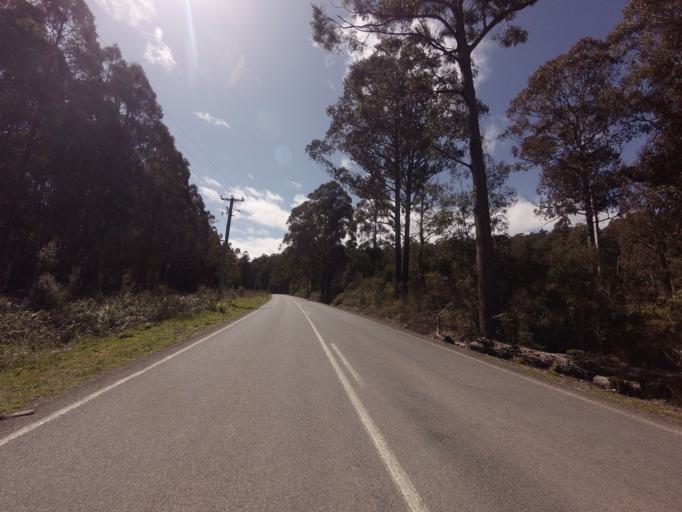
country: AU
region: Tasmania
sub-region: Derwent Valley
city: New Norfolk
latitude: -42.7169
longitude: 146.6905
